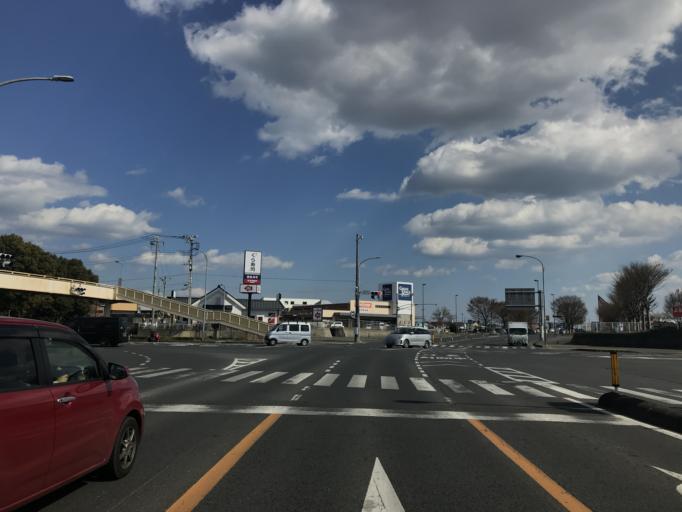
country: JP
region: Ibaraki
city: Mito-shi
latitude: 36.3411
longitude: 140.4812
